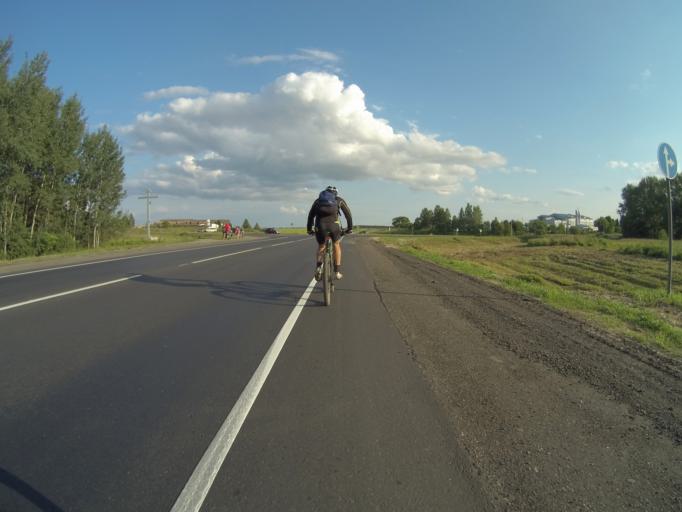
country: RU
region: Vladimir
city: Suzdal'
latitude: 56.4239
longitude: 40.4765
